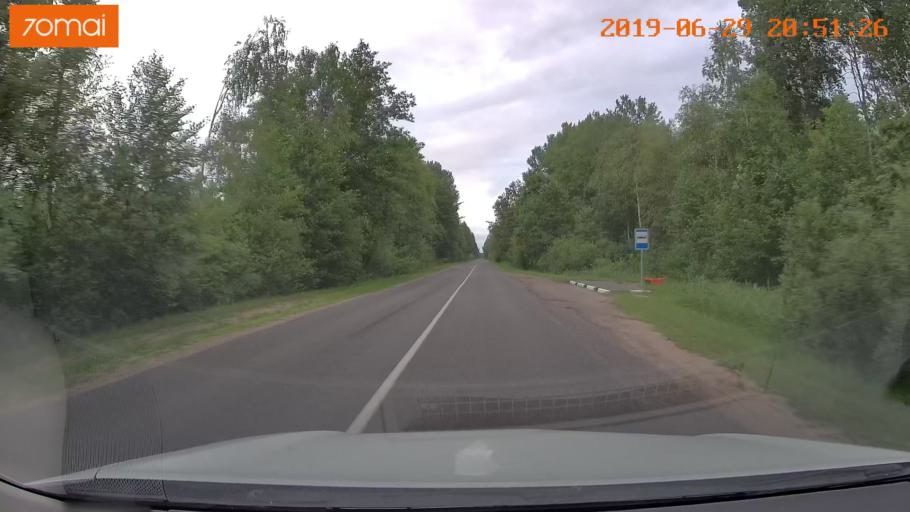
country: BY
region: Brest
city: Hantsavichy
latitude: 52.6881
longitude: 26.3494
